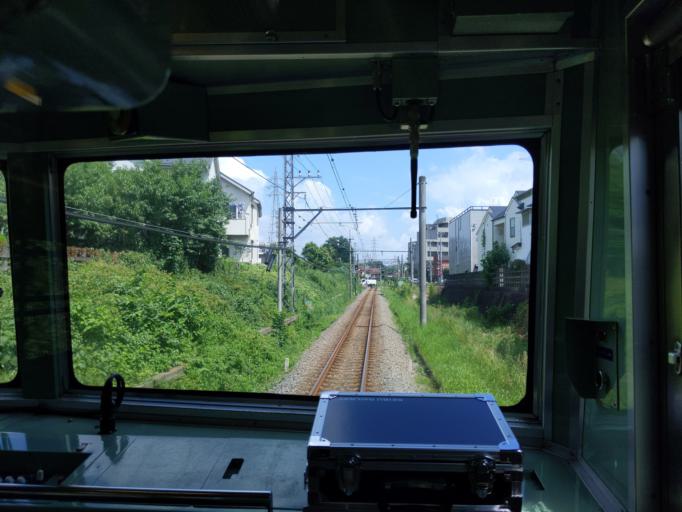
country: JP
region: Tokyo
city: Kamirenjaku
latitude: 35.6934
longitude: 139.5246
